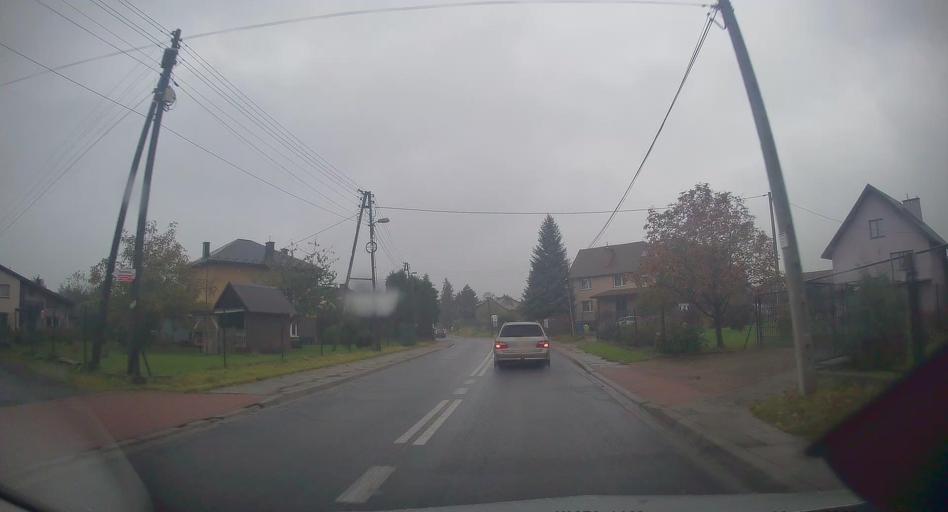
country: PL
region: Lesser Poland Voivodeship
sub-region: Powiat krakowski
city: Ochojno
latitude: 49.9789
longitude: 19.9885
